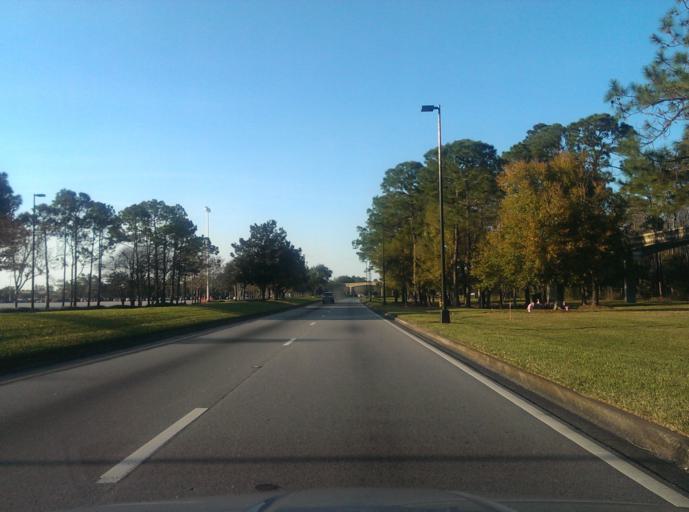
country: US
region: Florida
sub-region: Osceola County
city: Celebration
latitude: 28.3987
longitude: -81.5734
